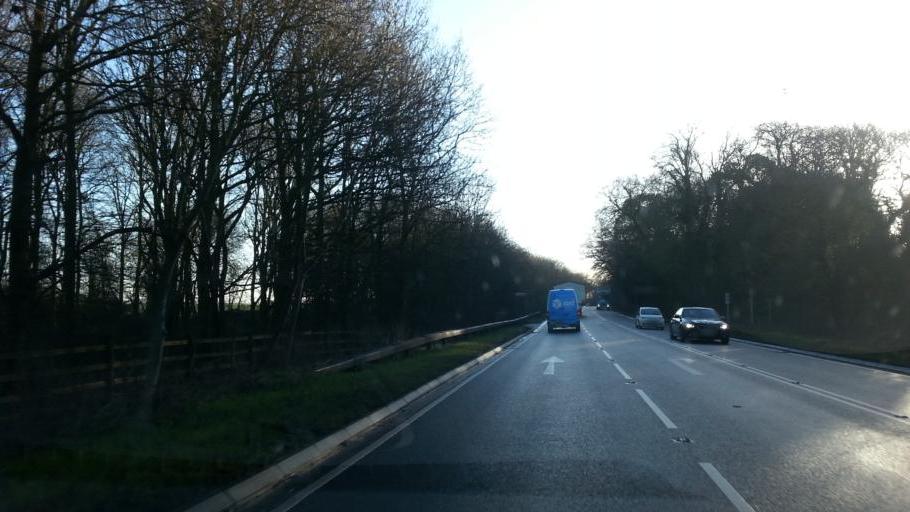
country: GB
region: England
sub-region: Nottinghamshire
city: South Collingham
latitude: 53.0806
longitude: -0.7185
